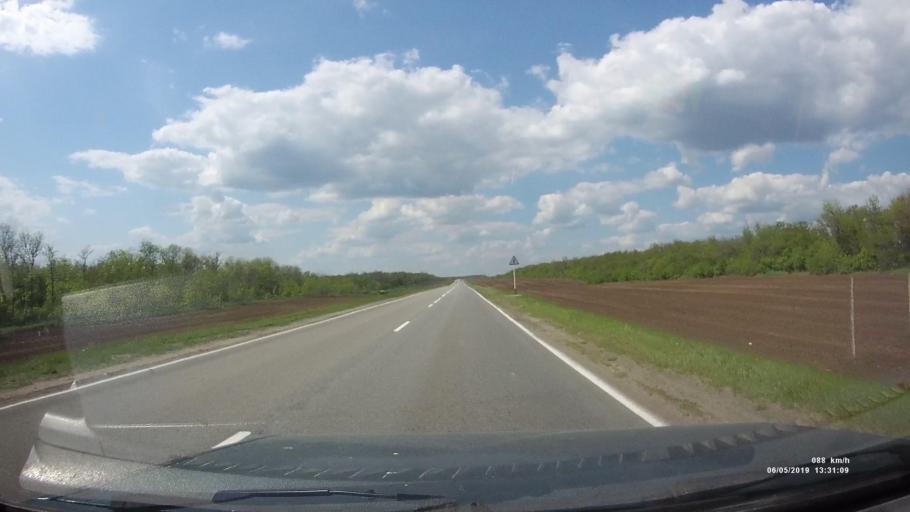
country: RU
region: Rostov
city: Ust'-Donetskiy
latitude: 47.6745
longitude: 40.8150
